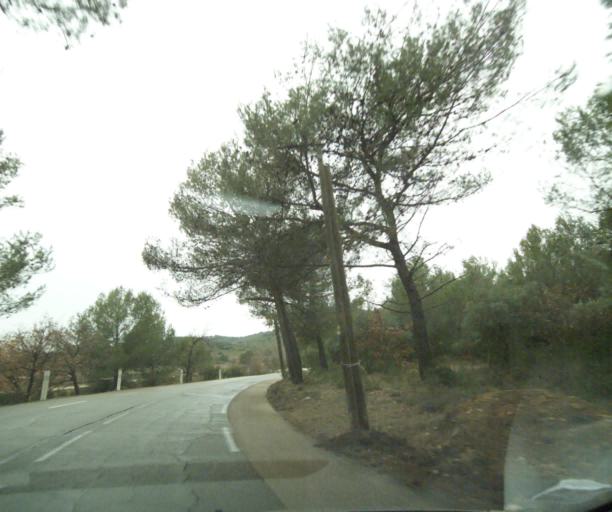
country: FR
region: Provence-Alpes-Cote d'Azur
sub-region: Departement des Bouches-du-Rhone
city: Le Puy-Sainte-Reparade
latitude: 43.6594
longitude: 5.4002
